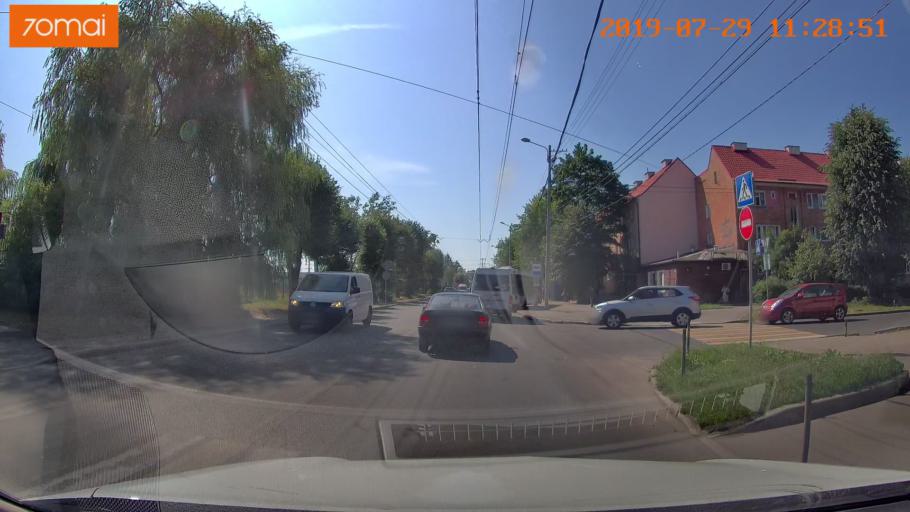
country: RU
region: Kaliningrad
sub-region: Gorod Kaliningrad
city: Kaliningrad
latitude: 54.6865
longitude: 20.5330
